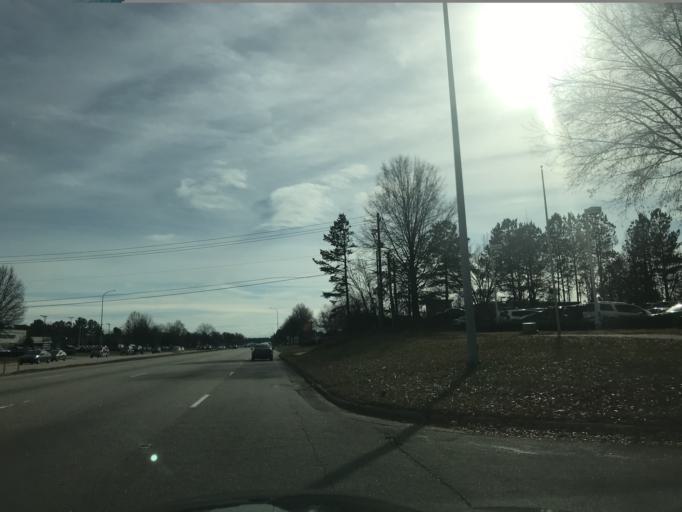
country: US
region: North Carolina
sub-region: Wake County
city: Raleigh
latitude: 35.8544
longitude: -78.5812
